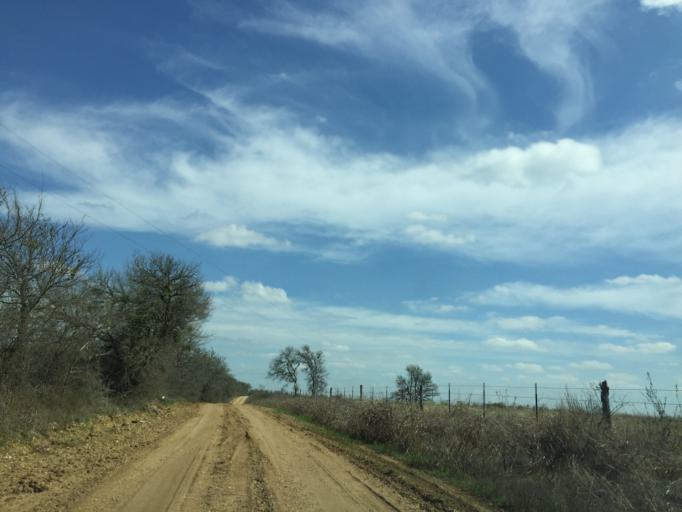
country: US
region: Texas
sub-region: Milam County
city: Thorndale
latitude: 30.5596
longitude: -97.1908
